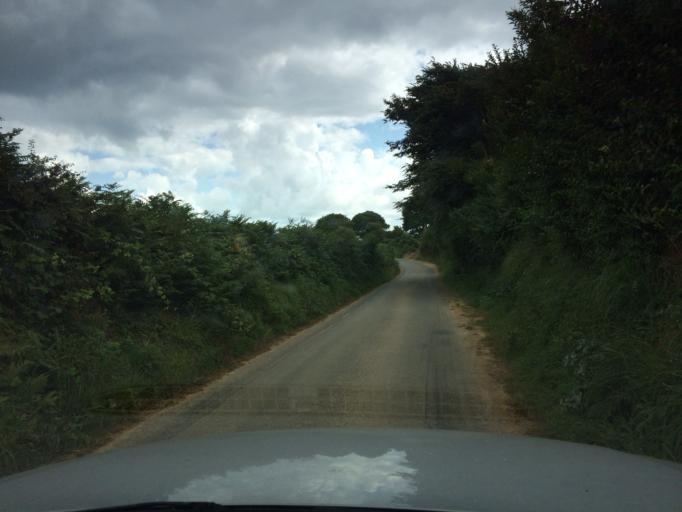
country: FR
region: Lower Normandy
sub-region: Departement de la Manche
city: Beaumont-Hague
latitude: 49.6871
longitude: -1.8805
